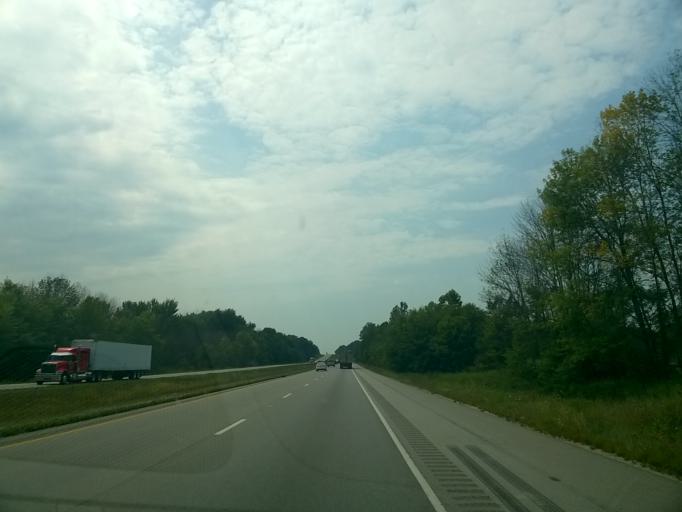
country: US
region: Indiana
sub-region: Clay County
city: Brazil
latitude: 39.4884
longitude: -86.9960
